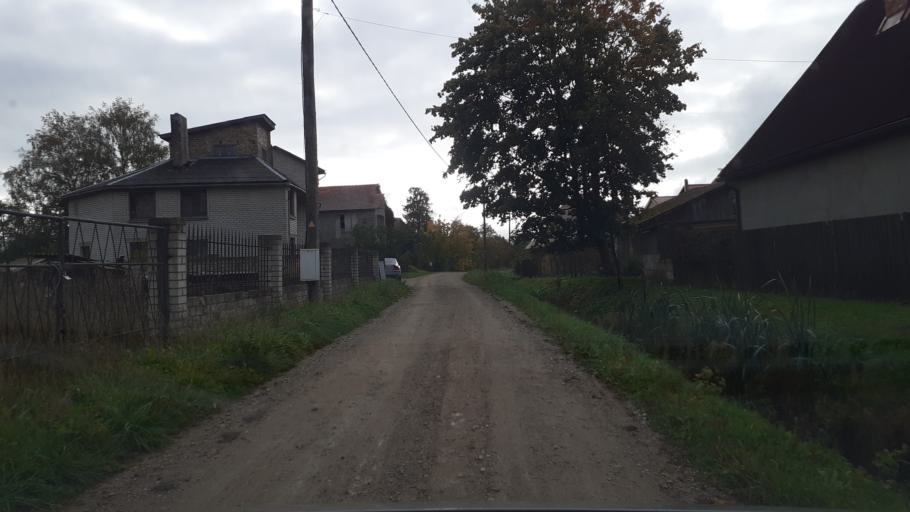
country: LV
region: Kuldigas Rajons
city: Kuldiga
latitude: 56.9654
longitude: 21.9908
